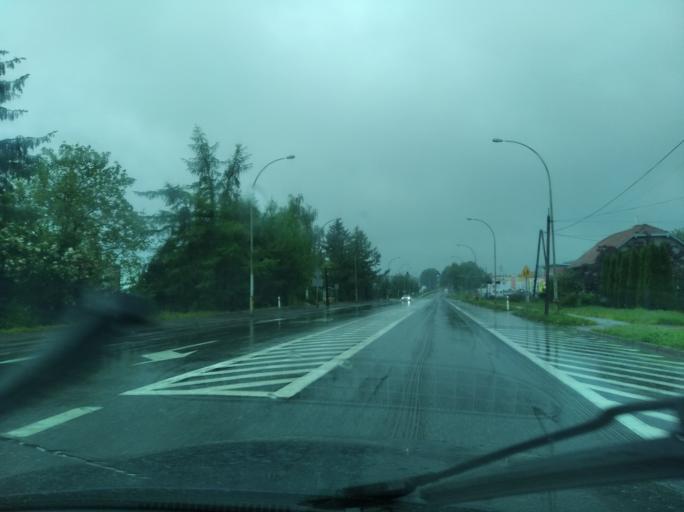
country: PL
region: Subcarpathian Voivodeship
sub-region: Powiat jasielski
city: Jaslo
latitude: 49.7561
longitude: 21.4938
